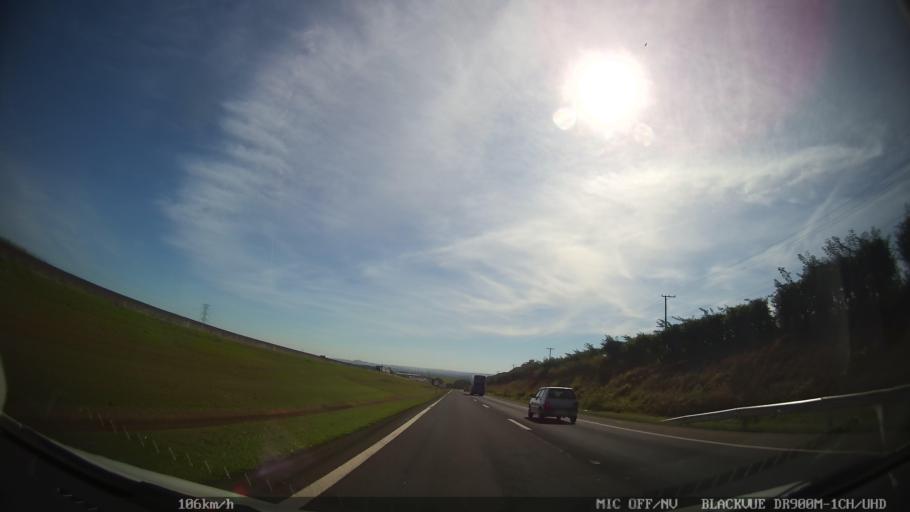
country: BR
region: Sao Paulo
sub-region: Leme
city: Leme
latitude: -22.2597
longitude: -47.3902
